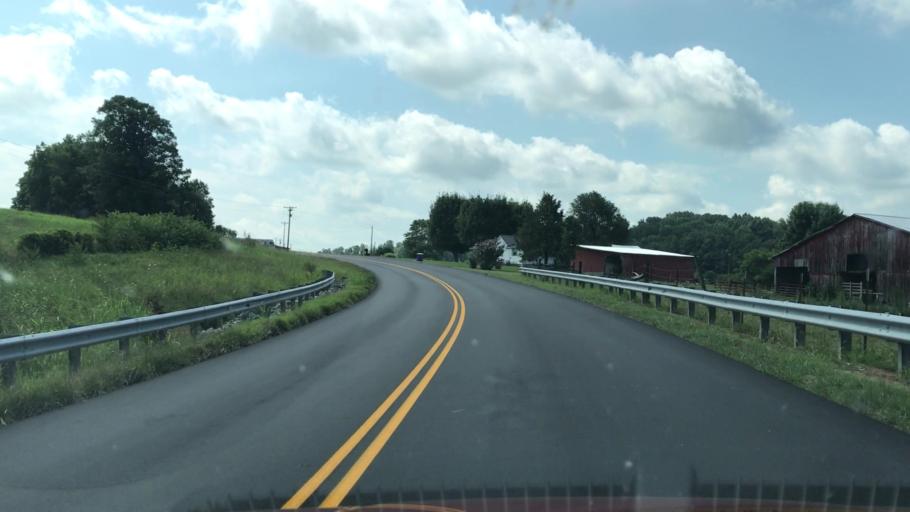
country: US
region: Kentucky
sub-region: Monroe County
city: Tompkinsville
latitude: 36.7669
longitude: -85.7992
